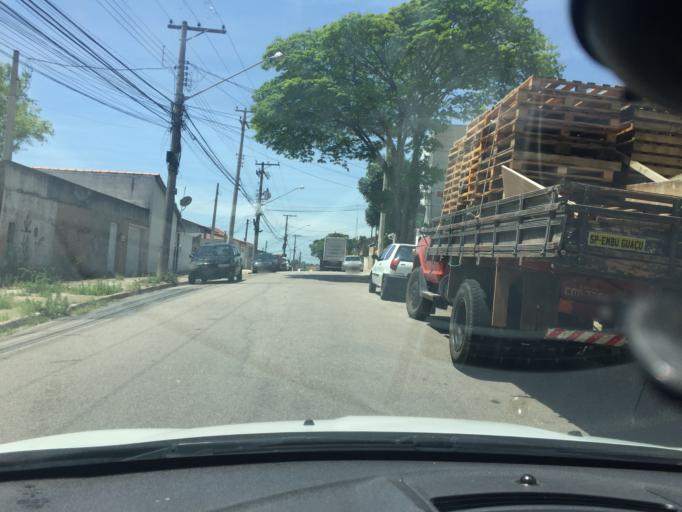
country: BR
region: Sao Paulo
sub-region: Jundiai
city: Jundiai
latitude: -23.2271
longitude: -46.8807
